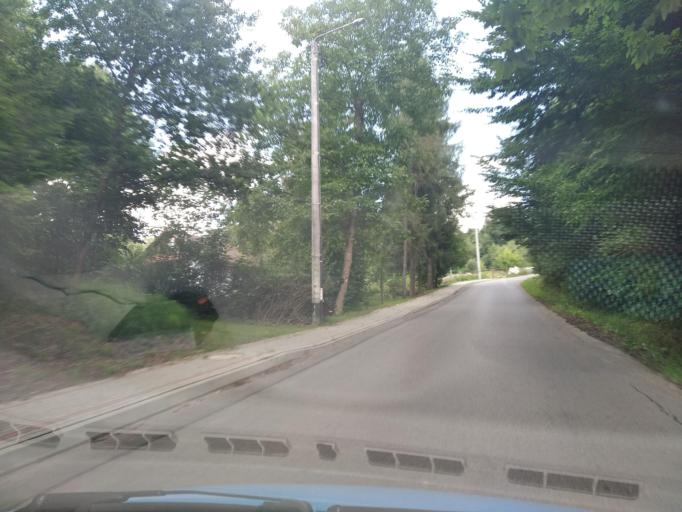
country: PL
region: Subcarpathian Voivodeship
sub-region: Powiat strzyzowski
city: Polomia
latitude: 49.9239
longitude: 21.9035
